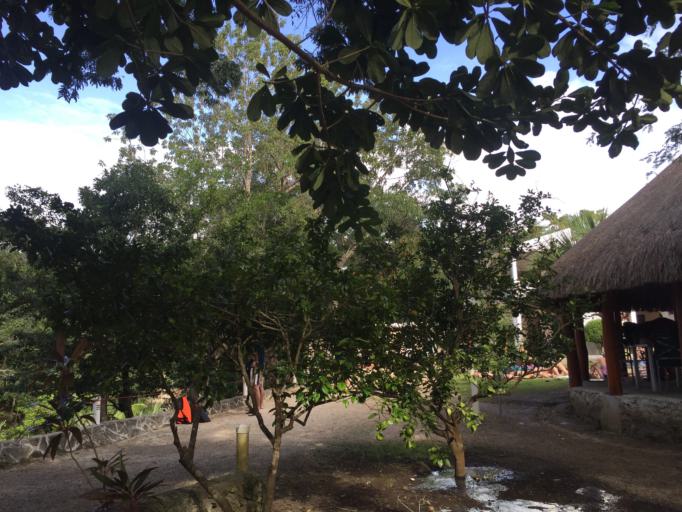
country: MX
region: Quintana Roo
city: Tulum
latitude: 20.2464
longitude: -87.4643
